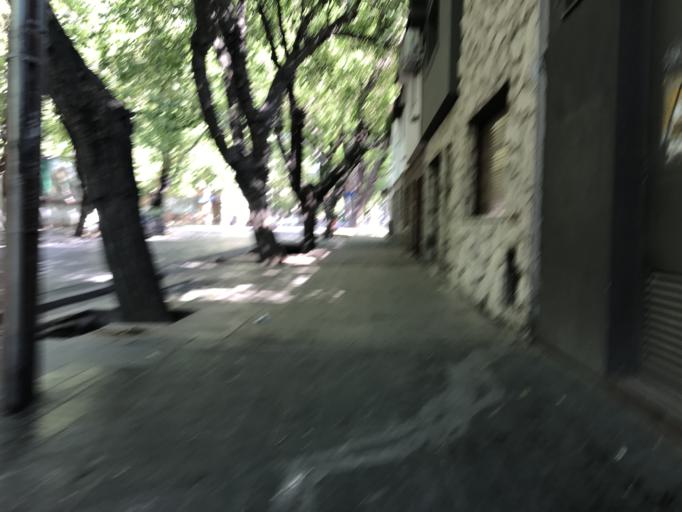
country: AR
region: Mendoza
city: Mendoza
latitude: -32.8924
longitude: -68.8474
